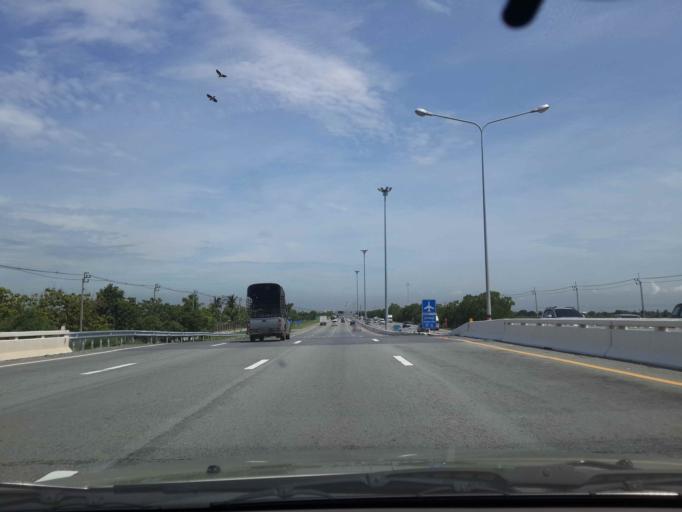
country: TH
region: Samut Prakan
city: Ban Khlong Bang Sao Thong
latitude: 13.6576
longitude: 100.8629
